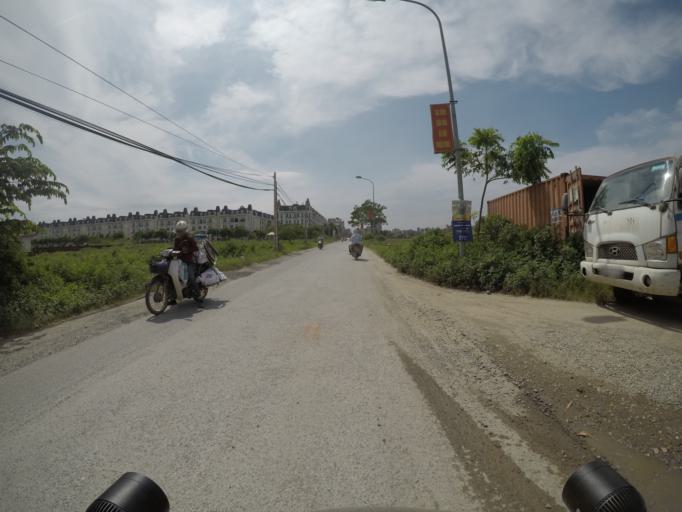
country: VN
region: Ha Noi
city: Troi
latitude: 21.0752
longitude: 105.7096
